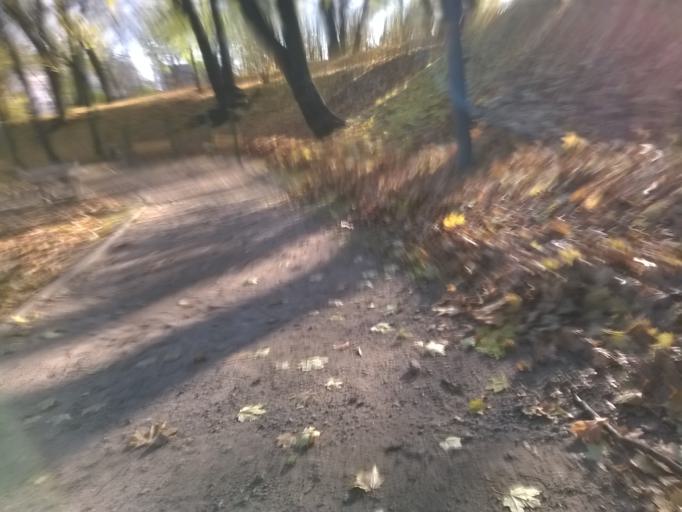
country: EE
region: Tartu
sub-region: Tartu linn
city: Tartu
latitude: 58.3787
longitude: 26.7216
